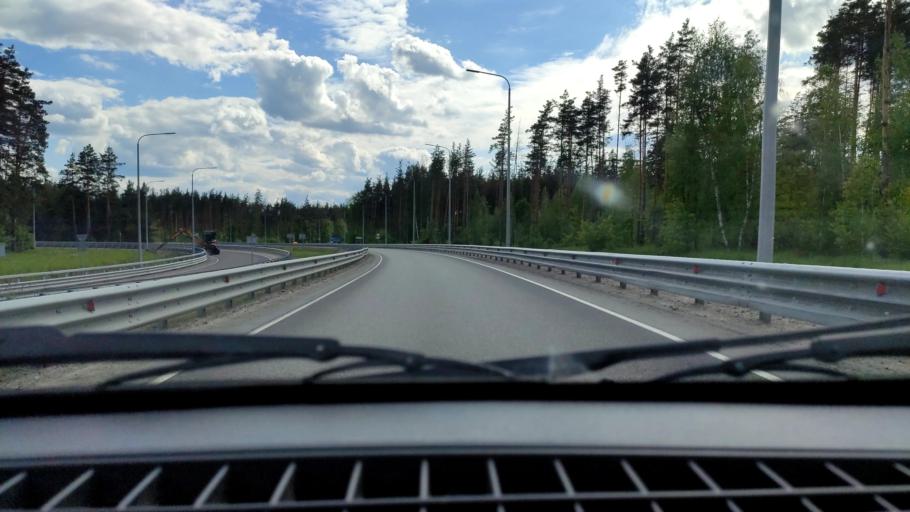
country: RU
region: Voronezj
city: Somovo
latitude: 51.6932
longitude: 39.3012
